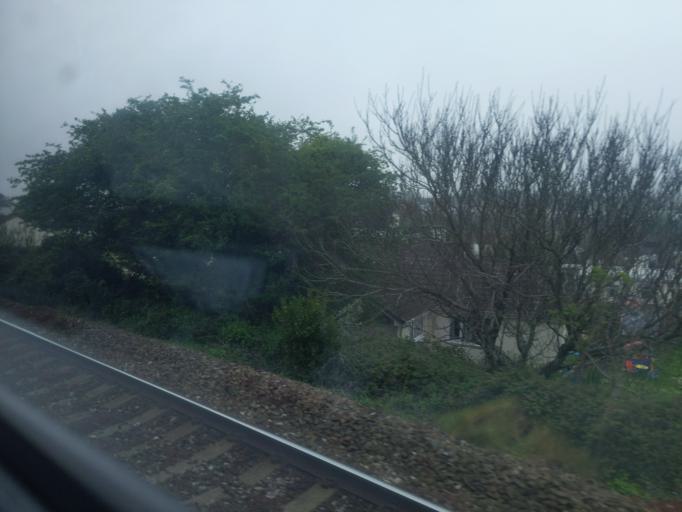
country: GB
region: England
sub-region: Cornwall
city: Hayle
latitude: 50.1877
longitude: -5.4159
